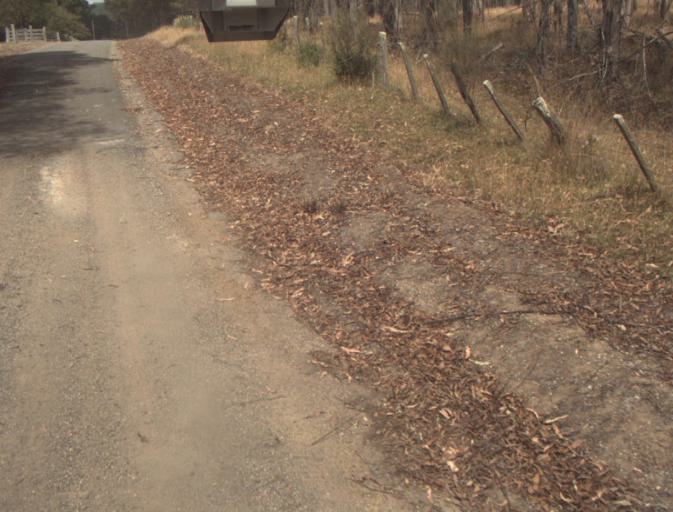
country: AU
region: Tasmania
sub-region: Dorset
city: Scottsdale
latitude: -41.4144
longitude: 147.5253
